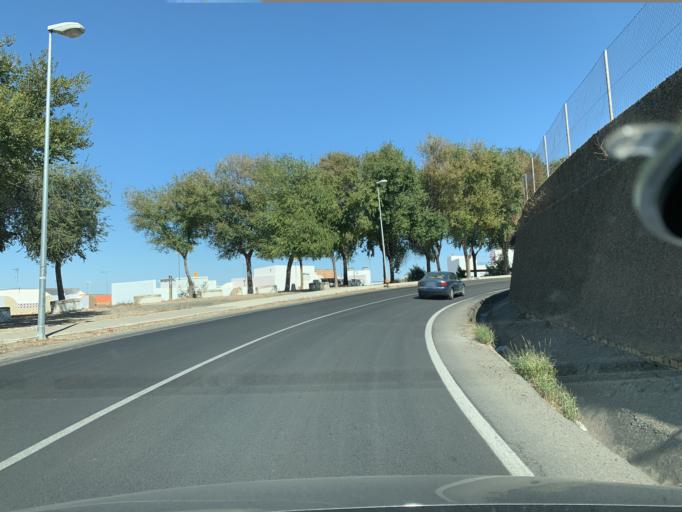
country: ES
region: Andalusia
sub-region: Provincia de Sevilla
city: Marchena
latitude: 37.3345
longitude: -5.4181
